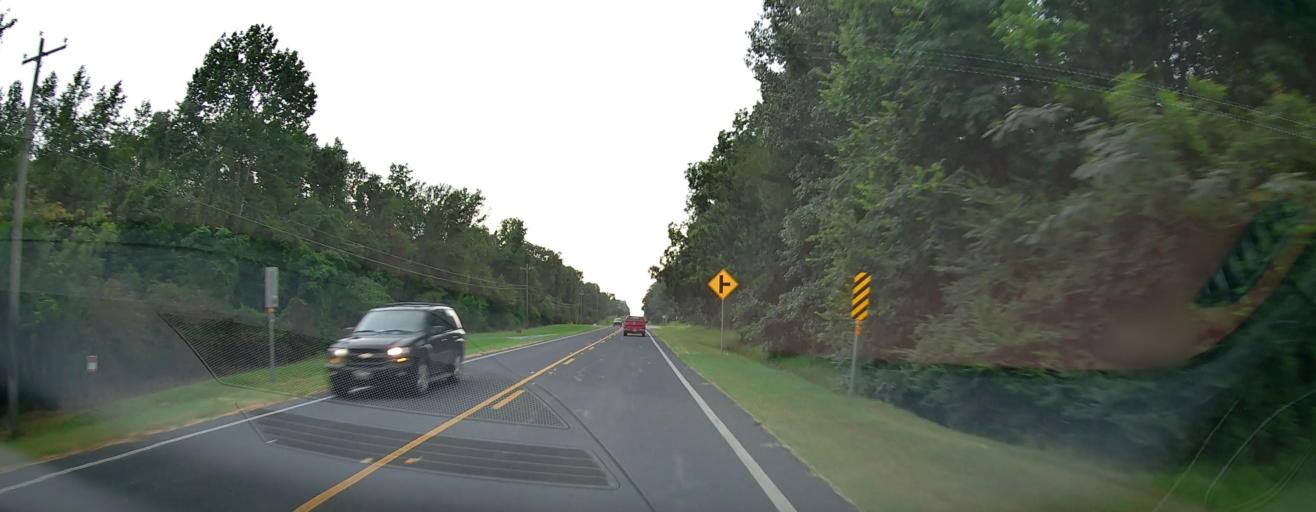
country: US
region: Georgia
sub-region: Laurens County
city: East Dublin
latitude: 32.5340
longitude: -82.8393
